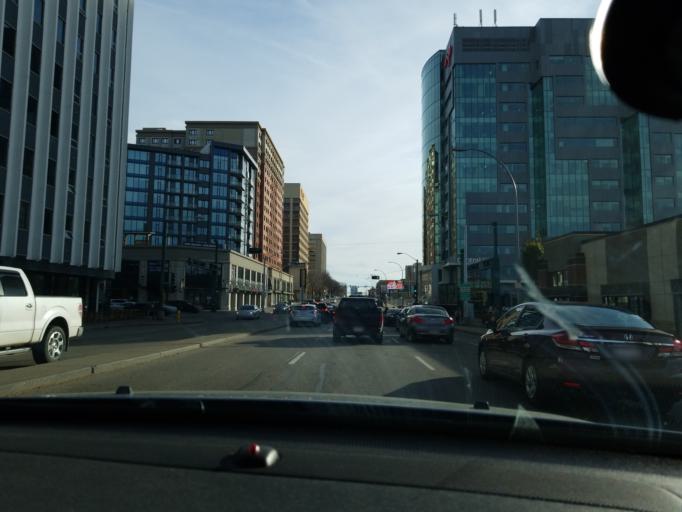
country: CA
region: Alberta
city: Edmonton
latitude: 53.5418
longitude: -113.5086
